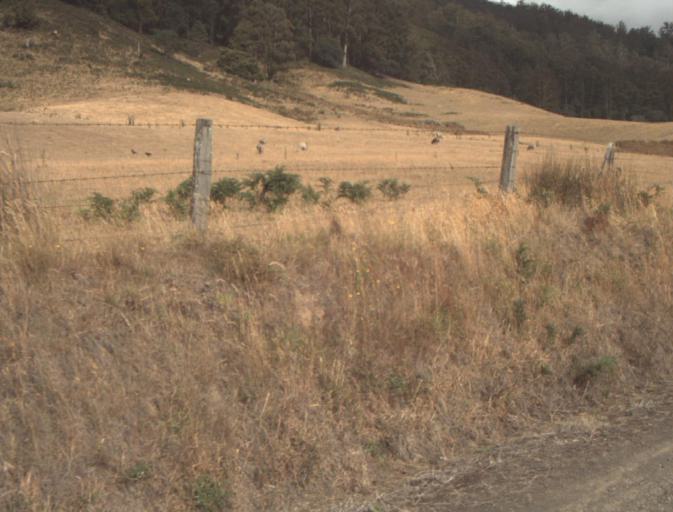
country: AU
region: Tasmania
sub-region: Dorset
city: Scottsdale
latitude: -41.4487
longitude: 147.5875
